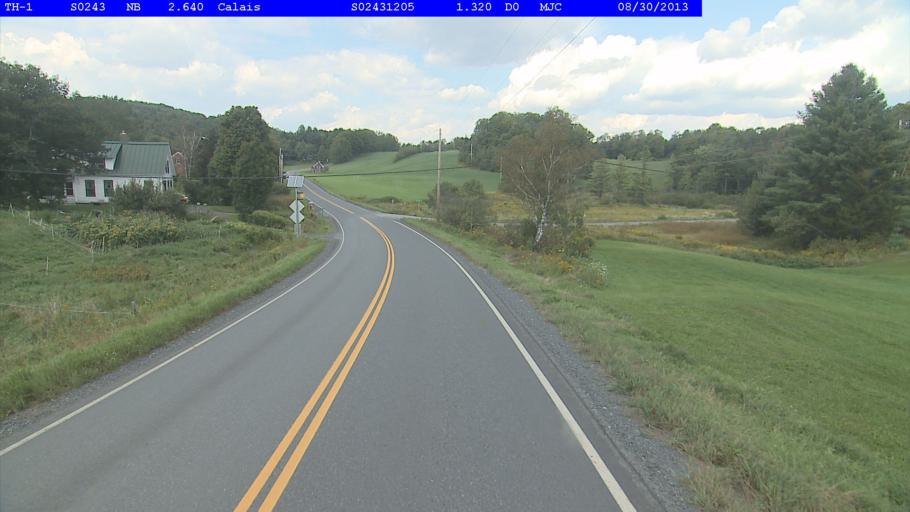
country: US
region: Vermont
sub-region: Washington County
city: Montpelier
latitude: 44.3521
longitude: -72.5108
